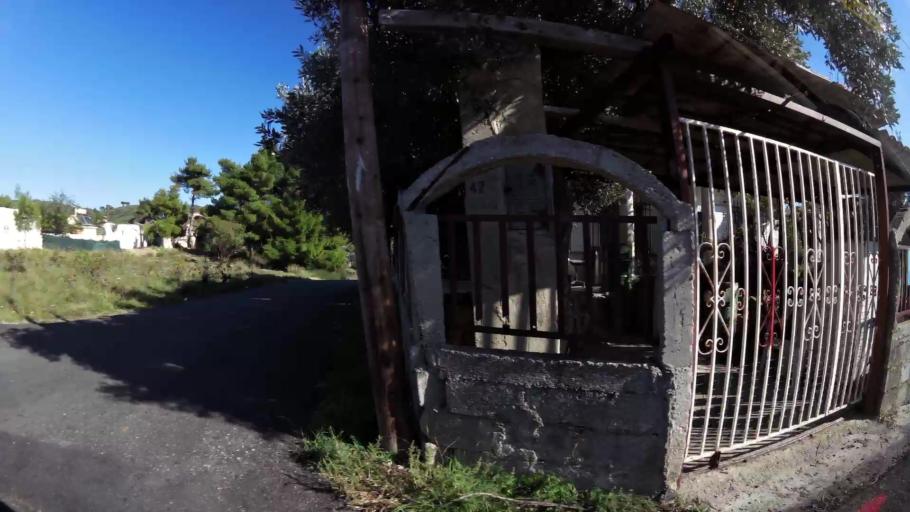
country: GR
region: Attica
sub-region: Nomarchia Anatolikis Attikis
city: Pallini
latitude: 38.0110
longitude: 23.8762
